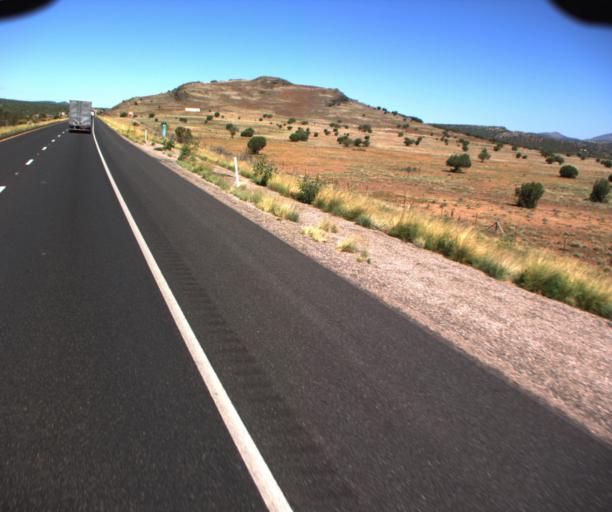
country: US
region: Arizona
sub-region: Yavapai County
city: Paulden
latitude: 35.2424
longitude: -112.6690
